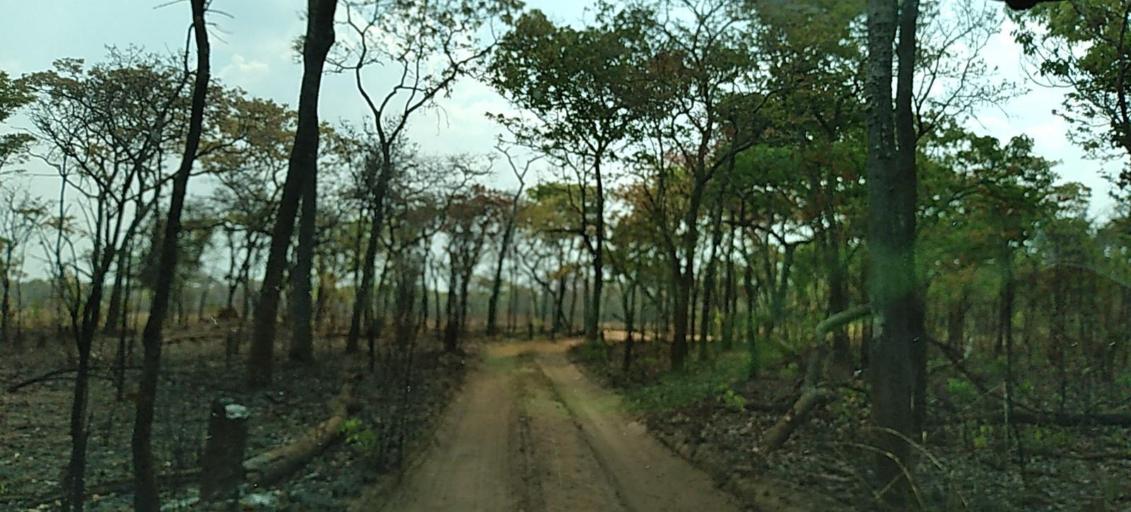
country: ZM
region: North-Western
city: Kabompo
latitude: -13.6171
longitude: 24.3710
